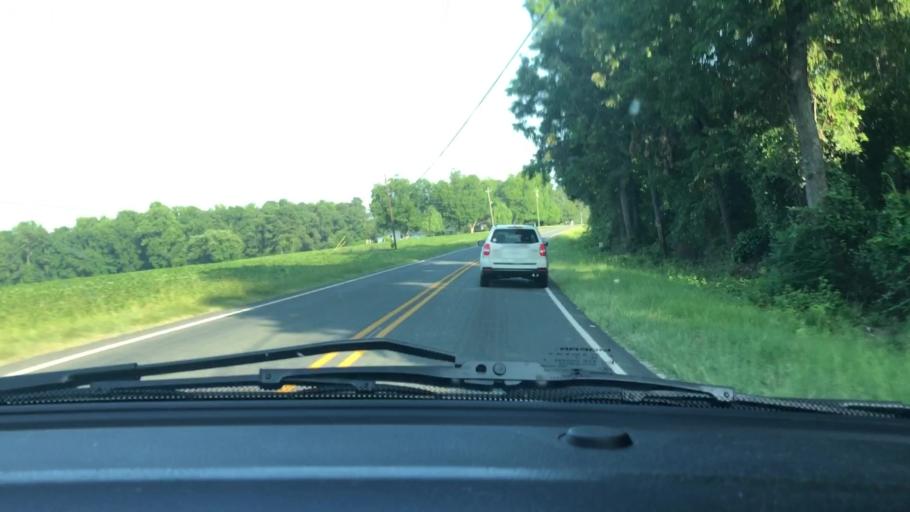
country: US
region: North Carolina
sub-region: Lee County
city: Broadway
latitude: 35.3565
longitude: -79.0791
